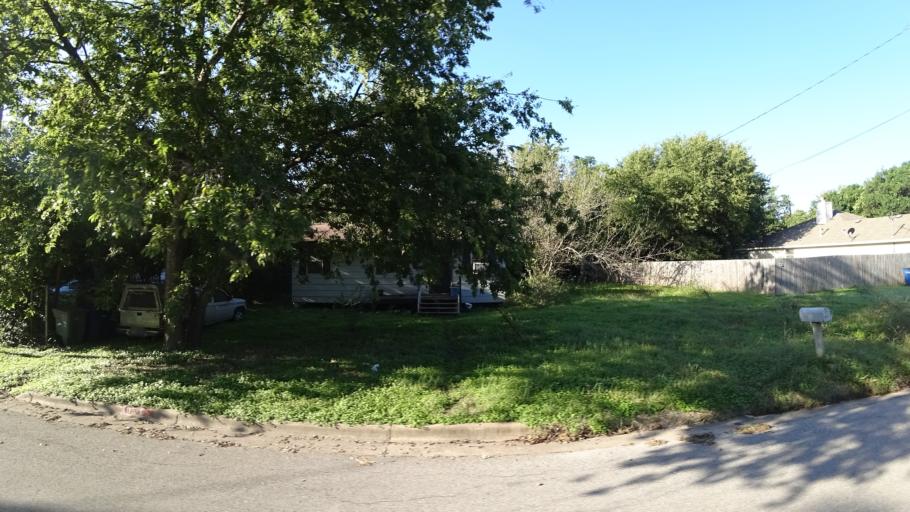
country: US
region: Texas
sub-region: Travis County
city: Wells Branch
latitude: 30.3573
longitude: -97.6928
